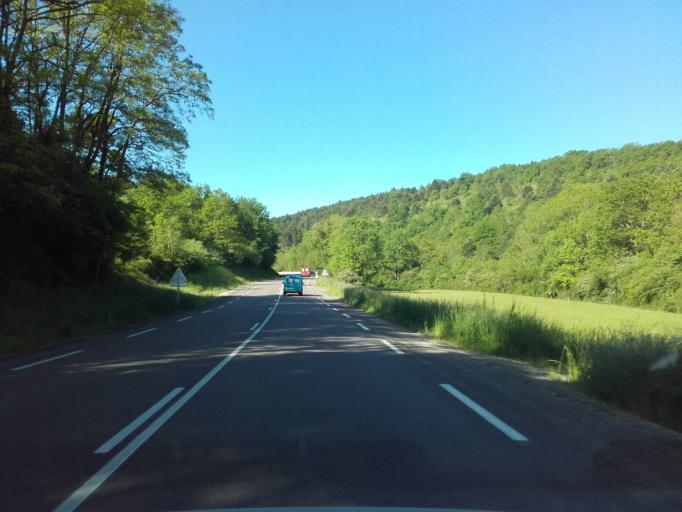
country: FR
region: Bourgogne
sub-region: Departement de la Cote-d'Or
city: Nolay
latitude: 46.9662
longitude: 4.6940
